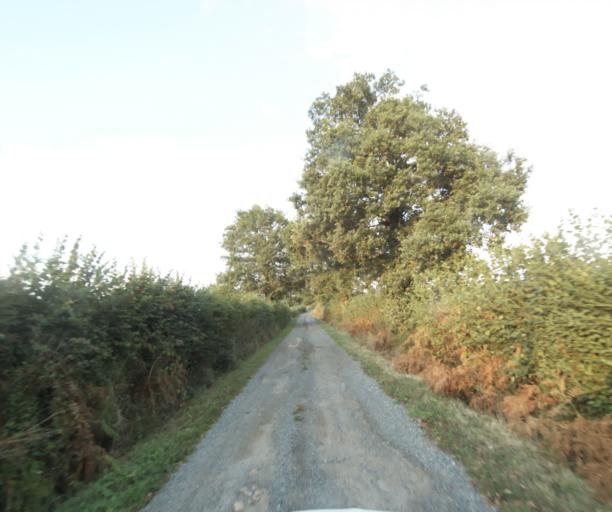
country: FR
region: Bourgogne
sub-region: Departement de Saone-et-Loire
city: Matour
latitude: 46.3970
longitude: 4.4149
